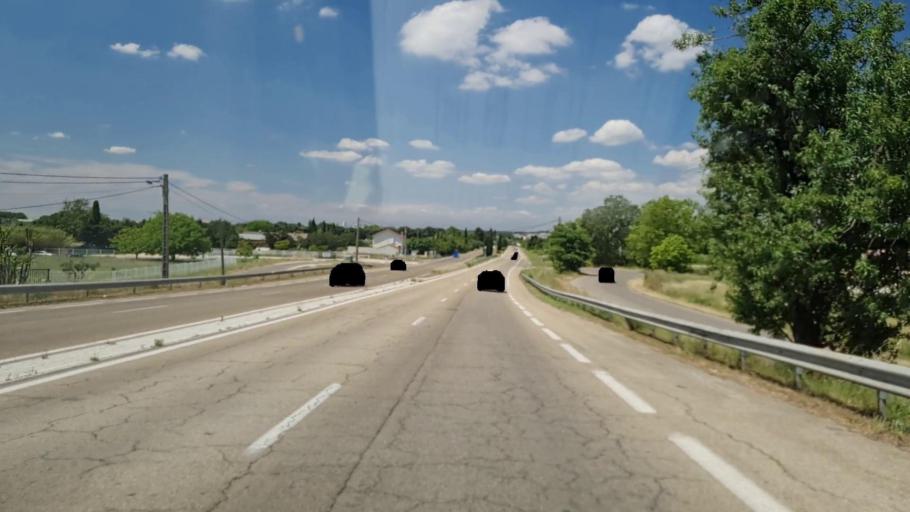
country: FR
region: Languedoc-Roussillon
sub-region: Departement du Gard
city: Rodilhan
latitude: 43.8354
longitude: 4.4050
